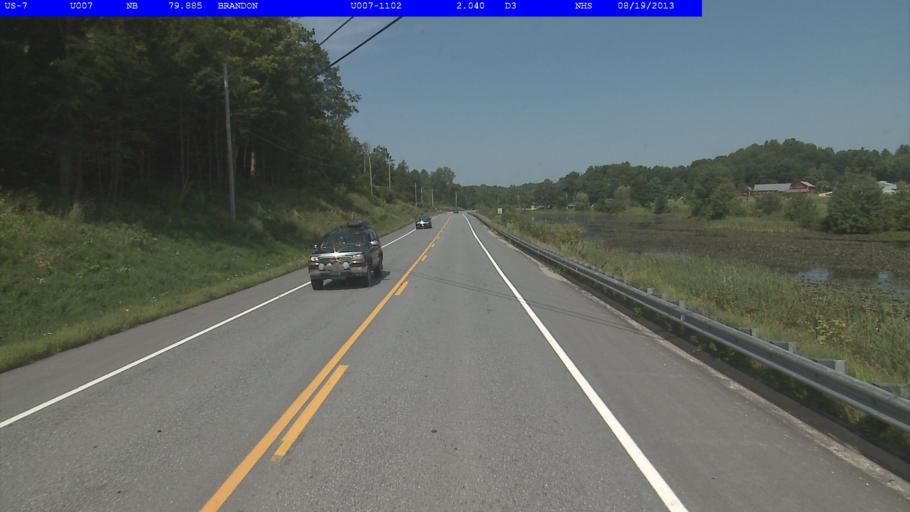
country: US
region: Vermont
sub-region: Rutland County
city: Brandon
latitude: 43.7817
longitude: -73.0603
